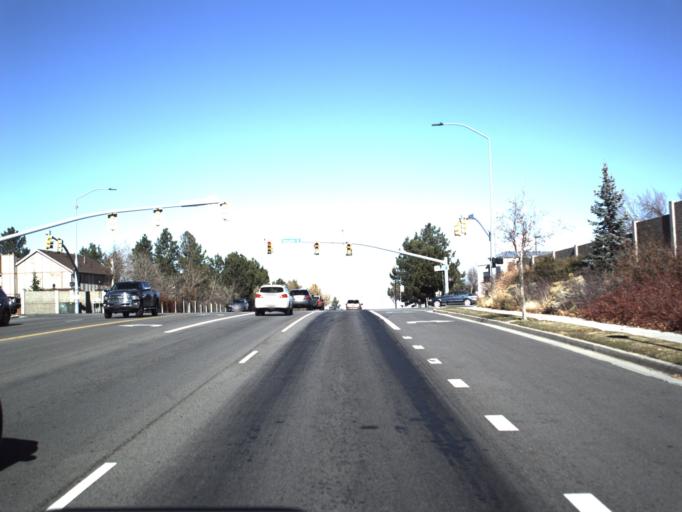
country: US
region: Utah
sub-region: Salt Lake County
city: Little Cottonwood Creek Valley
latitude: 40.5891
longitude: -111.8341
